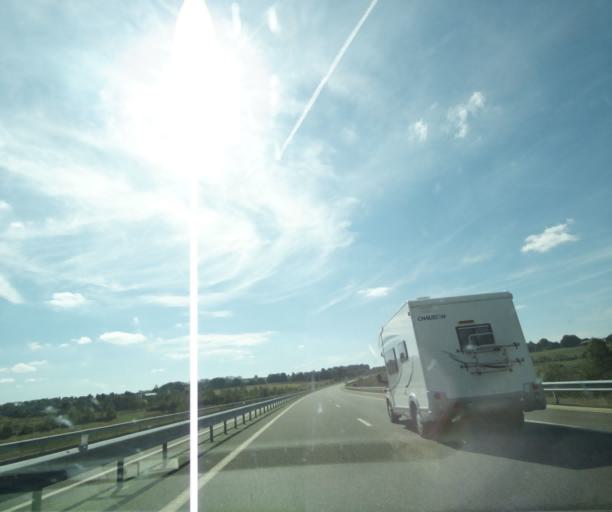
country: FR
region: Auvergne
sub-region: Departement du Puy-de-Dome
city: Saint-Sauves-d'Auvergne
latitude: 45.6801
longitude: 2.6940
